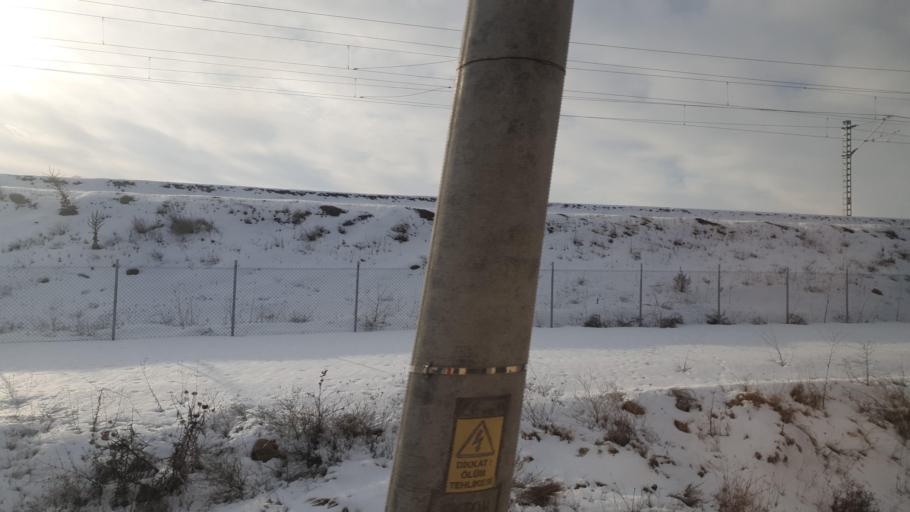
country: TR
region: Kirikkale
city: Baliseyh
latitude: 39.9282
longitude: 33.7891
